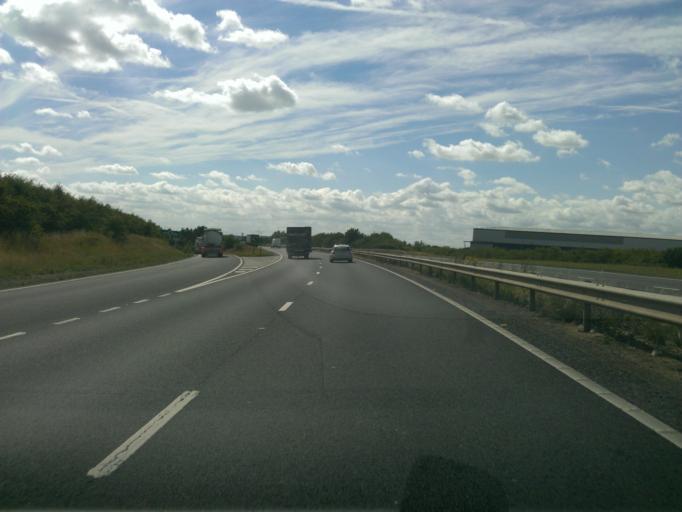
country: GB
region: England
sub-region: Northamptonshire
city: Thrapston
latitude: 52.3926
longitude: -0.5182
